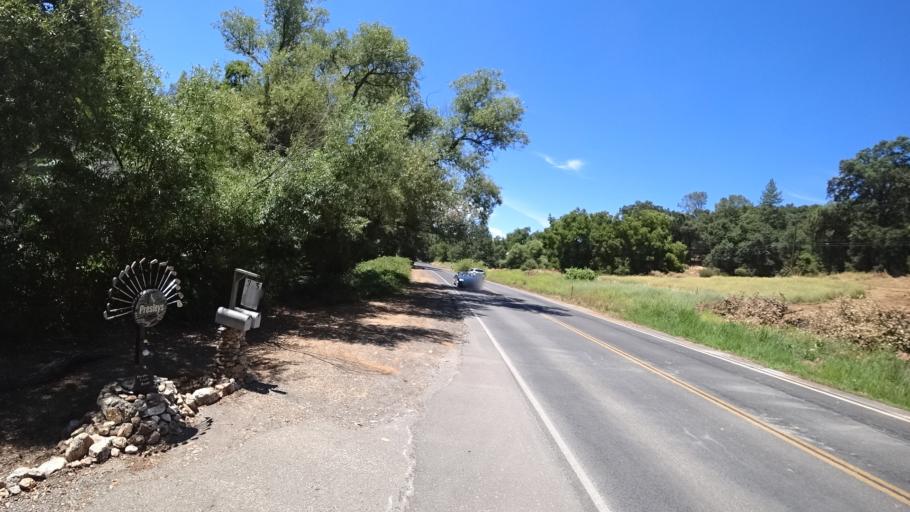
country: US
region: California
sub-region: Calaveras County
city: Murphys
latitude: 38.1141
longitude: -120.5036
